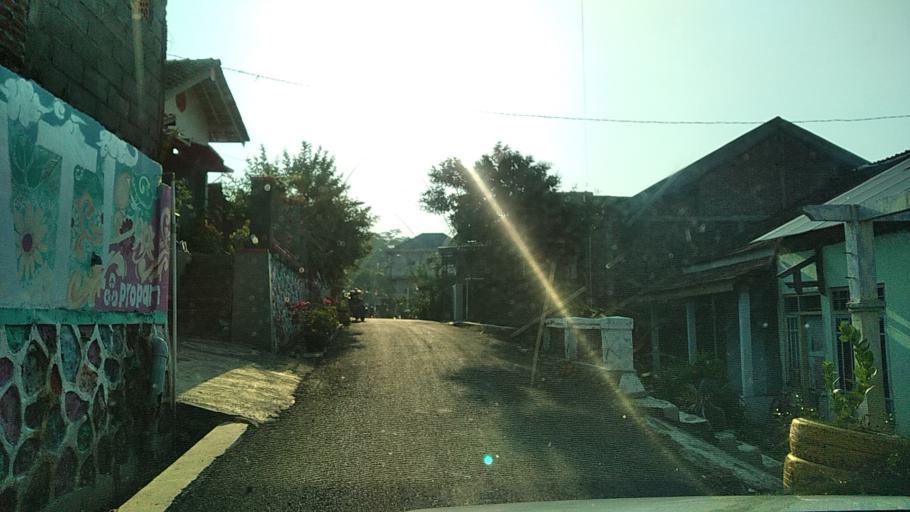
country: ID
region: Central Java
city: Ungaran
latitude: -7.0907
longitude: 110.3584
